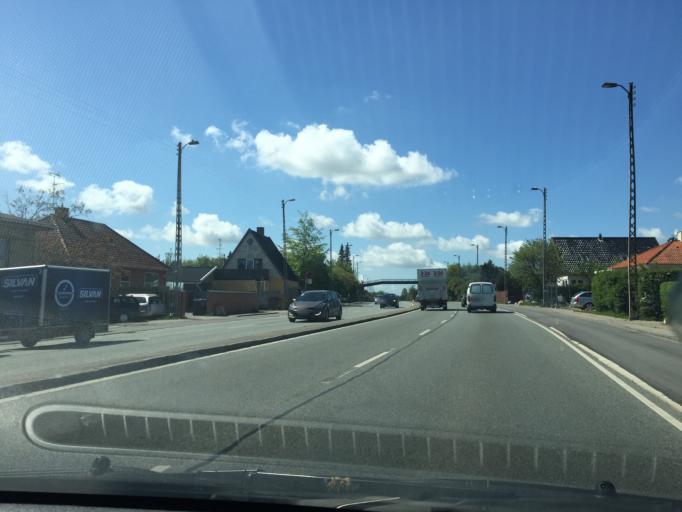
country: DK
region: Capital Region
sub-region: Rodovre Kommune
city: Rodovre
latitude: 55.6921
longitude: 12.4605
